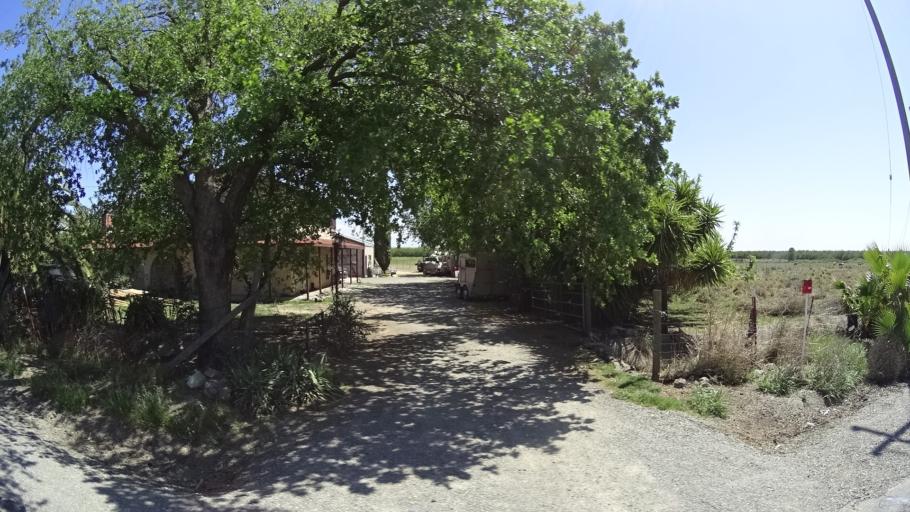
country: US
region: California
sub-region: Glenn County
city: Orland
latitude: 39.7418
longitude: -122.1409
